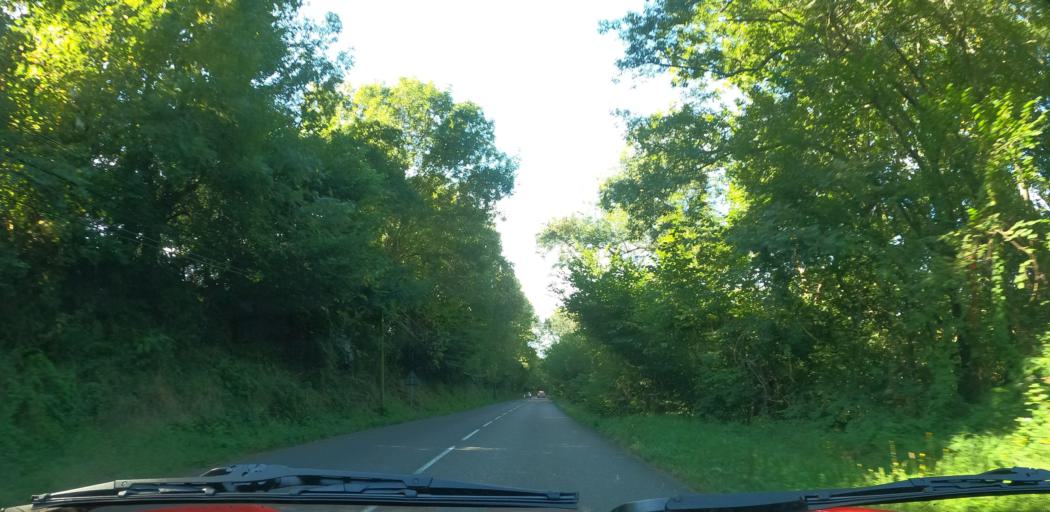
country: FR
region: Aquitaine
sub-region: Departement des Pyrenees-Atlantiques
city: Saint-Pee-sur-Nivelle
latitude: 43.3624
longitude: -1.5460
